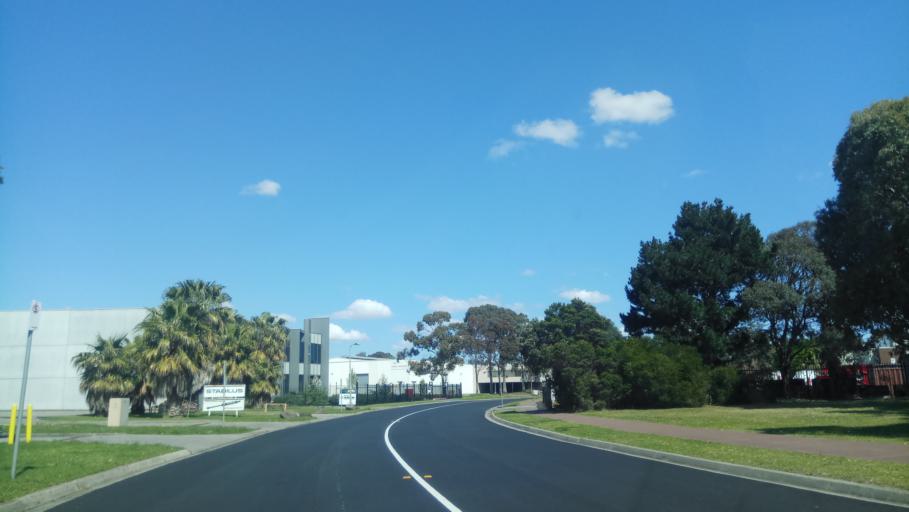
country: AU
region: Victoria
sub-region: Kingston
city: Dingley Village
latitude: -37.9850
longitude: 145.1148
